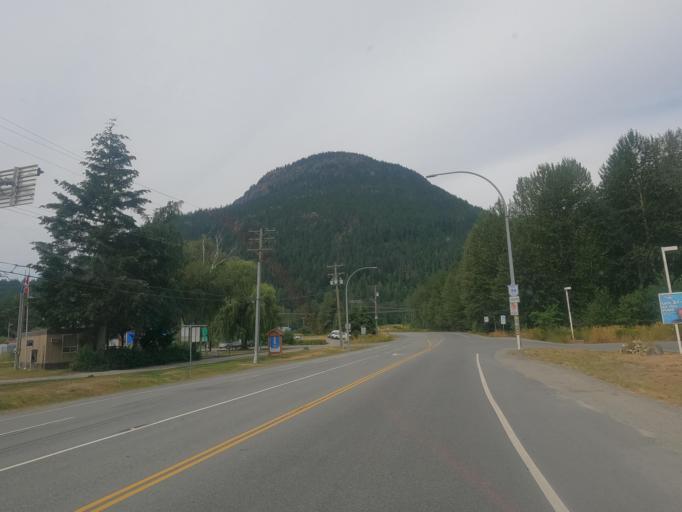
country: CA
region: British Columbia
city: Pemberton
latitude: 50.3183
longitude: -122.7964
